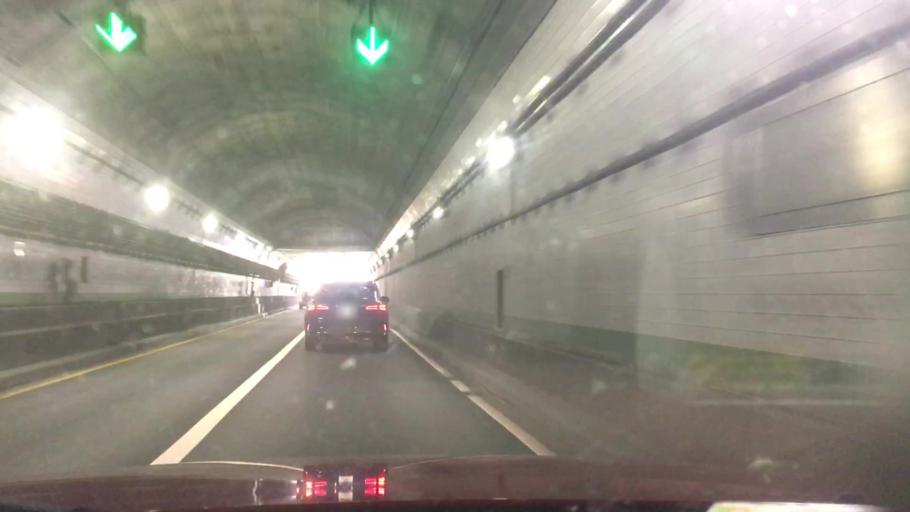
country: US
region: Virginia
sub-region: City of Portsmouth
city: Portsmouth
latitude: 36.8315
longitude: -76.2941
